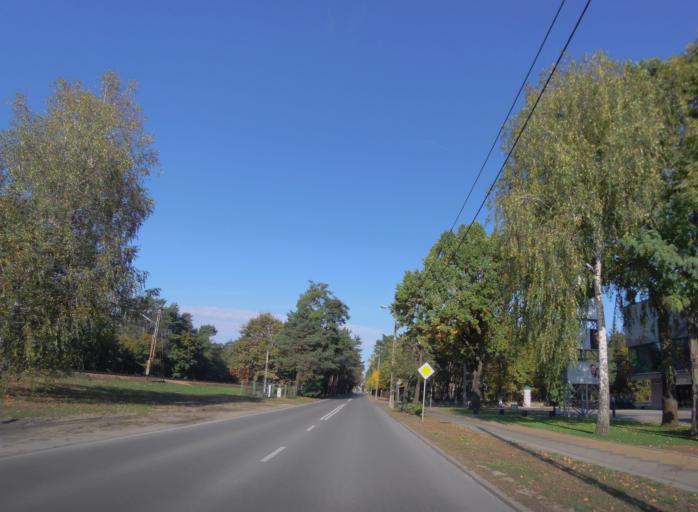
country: PL
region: Masovian Voivodeship
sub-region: Powiat otwocki
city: Jozefow
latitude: 52.1327
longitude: 21.2405
